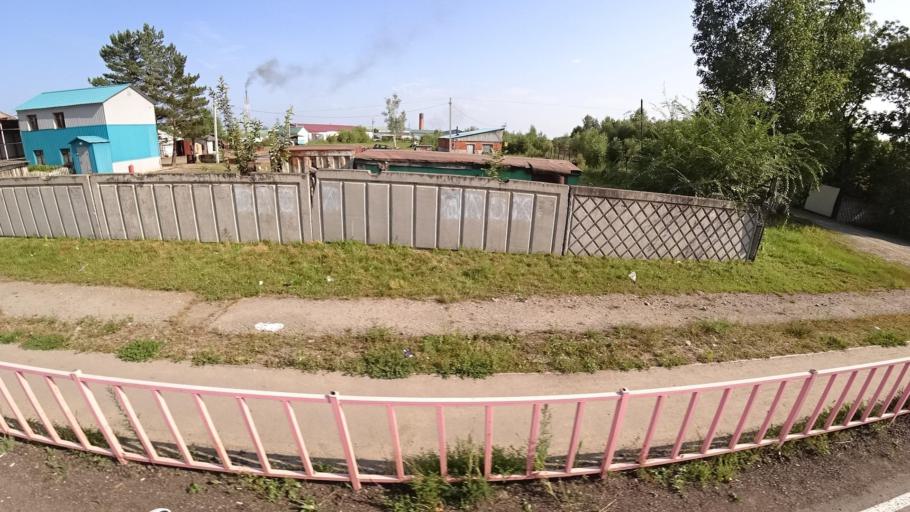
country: RU
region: Khabarovsk Krai
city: Khor
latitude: 47.9737
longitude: 135.0647
